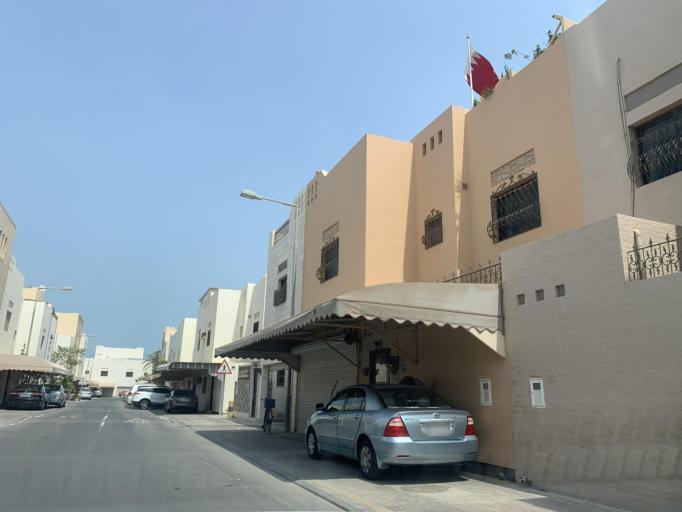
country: BH
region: Muharraq
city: Al Hadd
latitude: 26.2686
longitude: 50.6598
